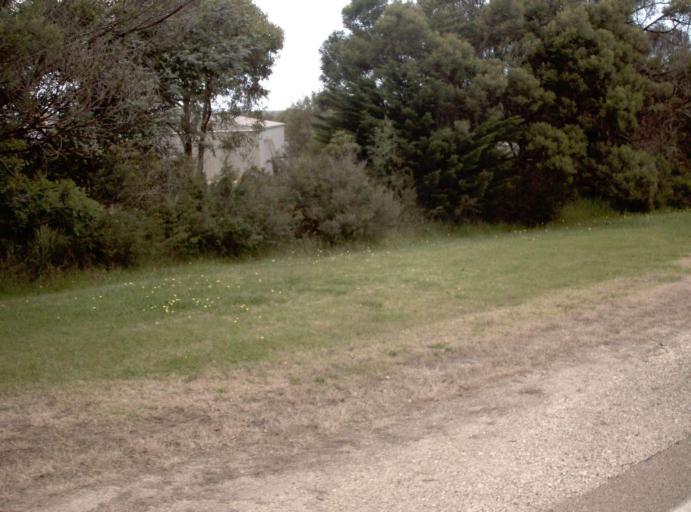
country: AU
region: Victoria
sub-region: Wellington
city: Sale
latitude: -38.1924
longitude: 147.0939
